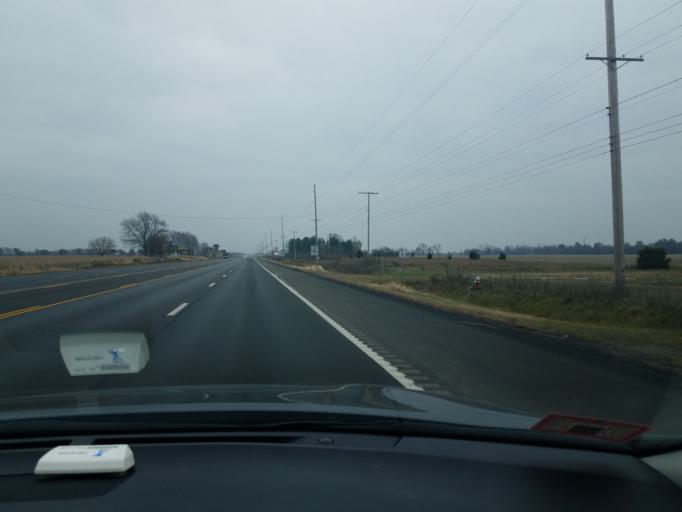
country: US
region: Ohio
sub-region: Erie County
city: Milan
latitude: 41.3723
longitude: -82.6417
